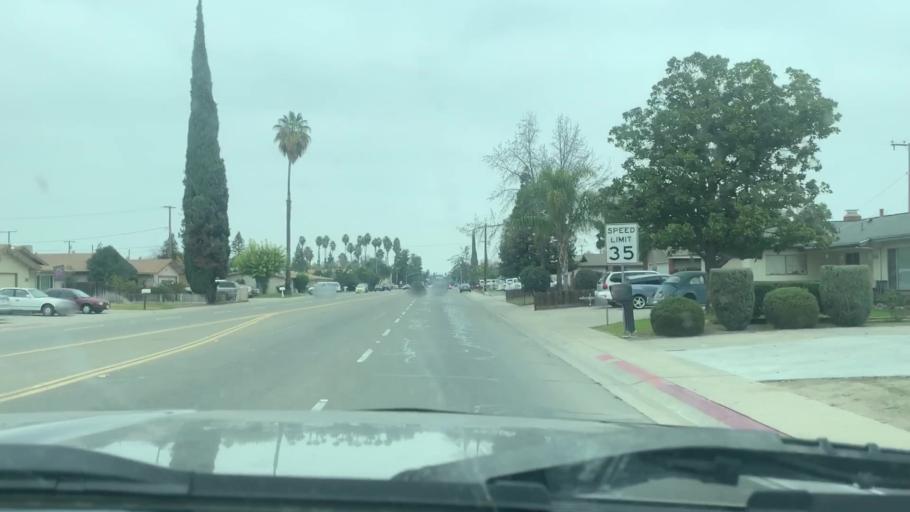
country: US
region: California
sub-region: Tulare County
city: Visalia
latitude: 36.3210
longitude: -119.3317
